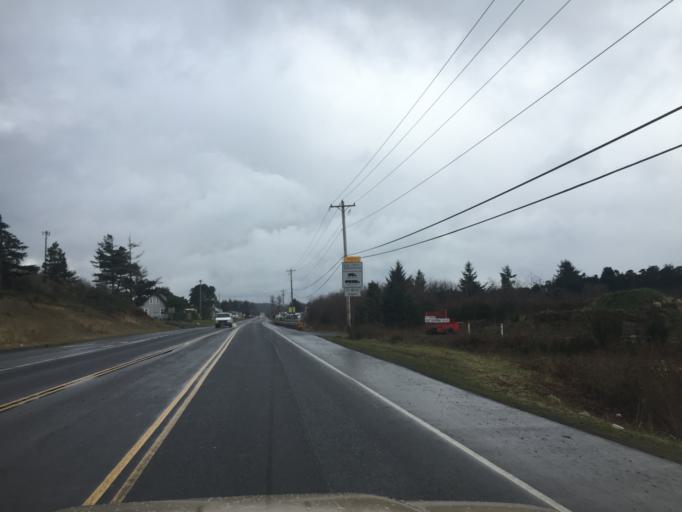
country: US
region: Oregon
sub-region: Lincoln County
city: Newport
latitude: 44.6090
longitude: -124.0524
